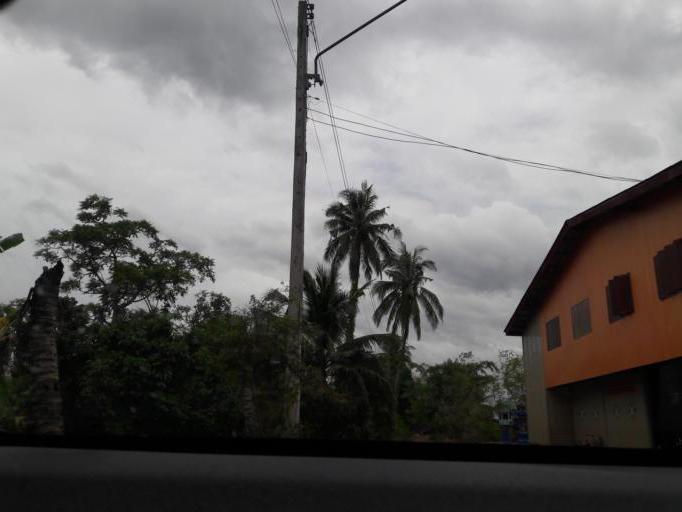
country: TH
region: Ratchaburi
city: Damnoen Saduak
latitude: 13.5692
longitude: 99.9957
